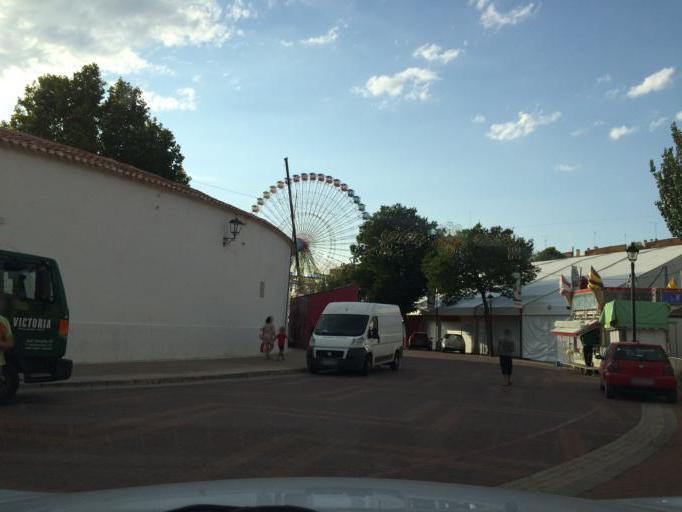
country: ES
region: Castille-La Mancha
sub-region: Provincia de Albacete
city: Albacete
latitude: 38.9972
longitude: -1.8681
